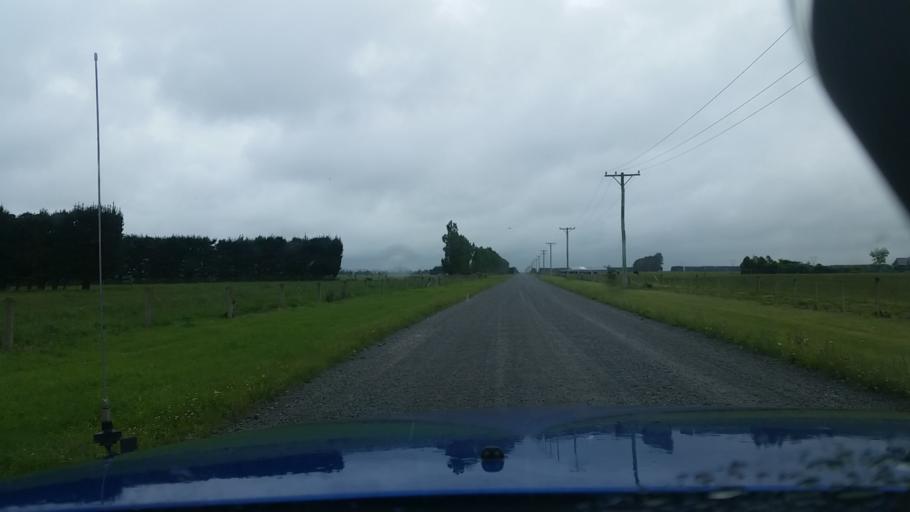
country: NZ
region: Canterbury
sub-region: Ashburton District
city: Tinwald
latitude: -43.8839
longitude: 171.5178
